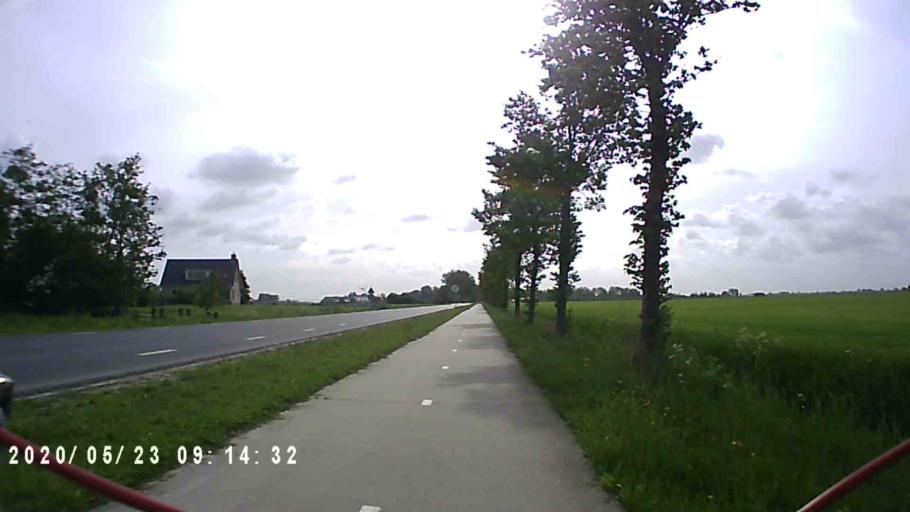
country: NL
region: Groningen
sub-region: Gemeente Bedum
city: Bedum
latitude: 53.3027
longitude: 6.6368
